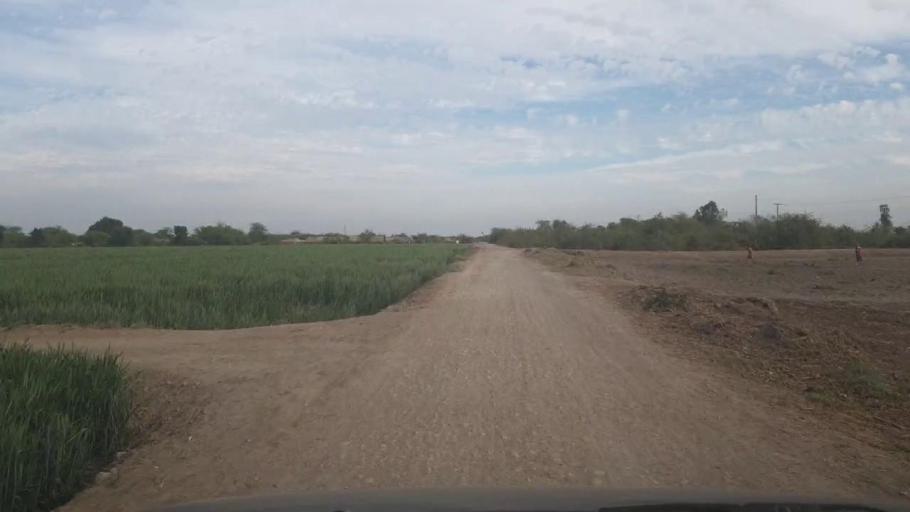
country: PK
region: Sindh
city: Samaro
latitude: 25.3306
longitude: 69.2589
